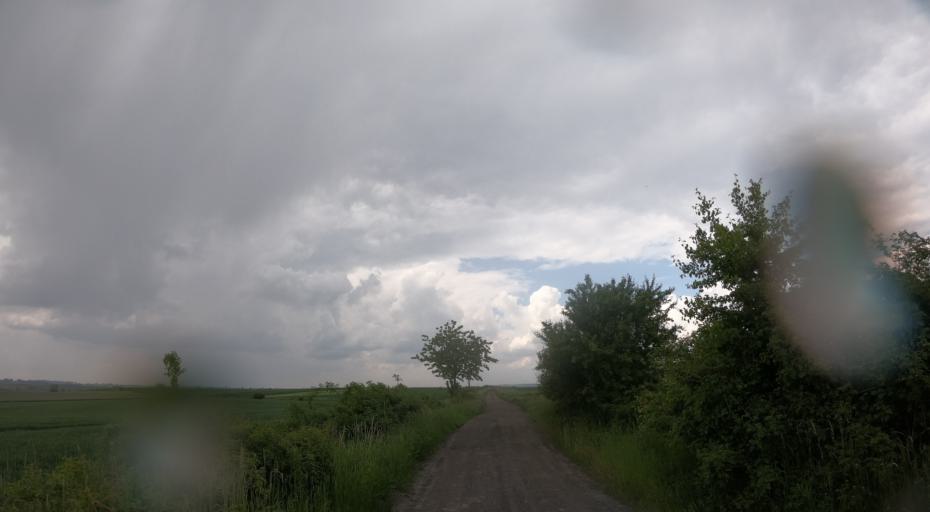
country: PL
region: West Pomeranian Voivodeship
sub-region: Powiat pyrzycki
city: Bielice
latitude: 53.2478
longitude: 14.7173
